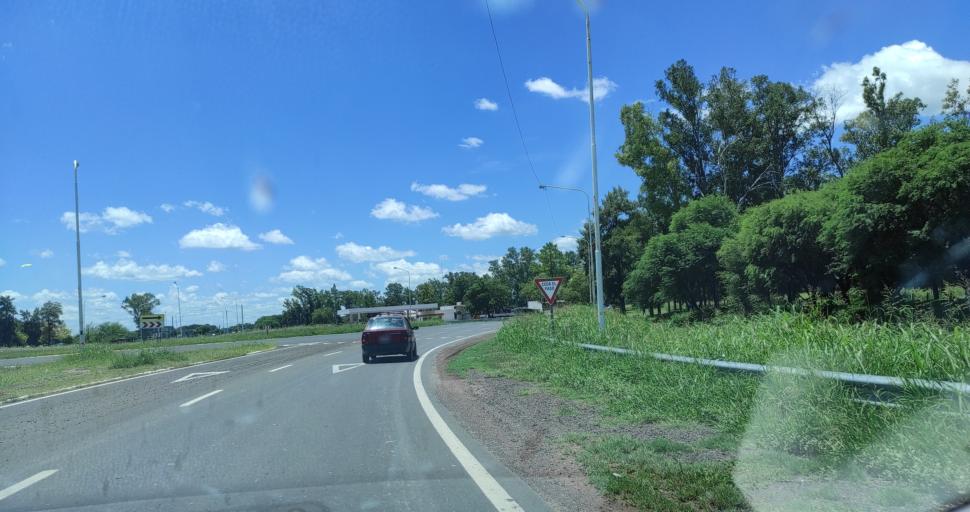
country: AR
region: Chaco
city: Avia Terai
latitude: -26.7066
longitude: -60.7480
